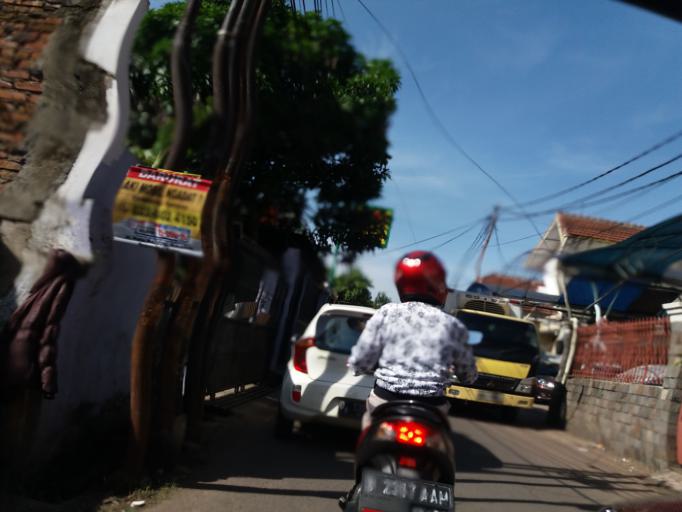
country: ID
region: West Java
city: Bandung
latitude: -6.9440
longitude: 107.6094
